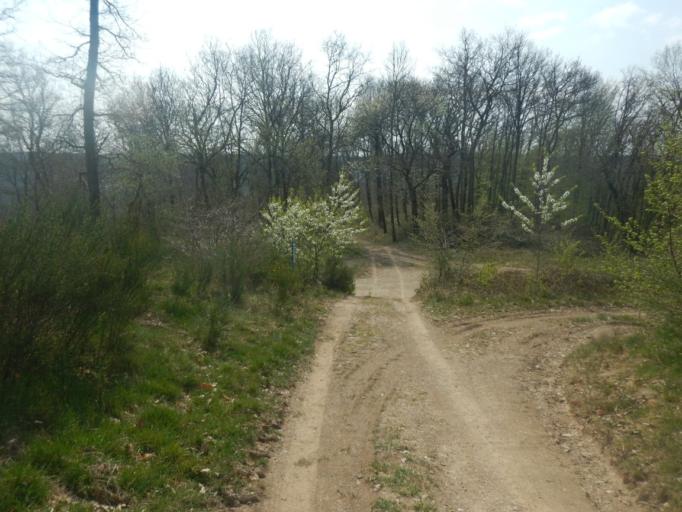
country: LU
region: Diekirch
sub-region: Canton de Wiltz
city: Esch-sur-Sure
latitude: 49.9123
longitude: 5.9147
